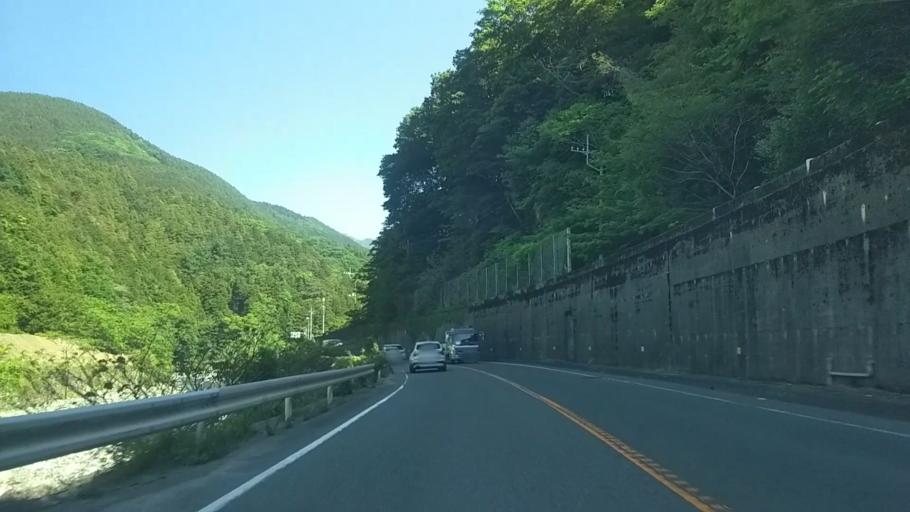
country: JP
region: Shizuoka
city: Fujinomiya
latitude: 35.3286
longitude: 138.4286
